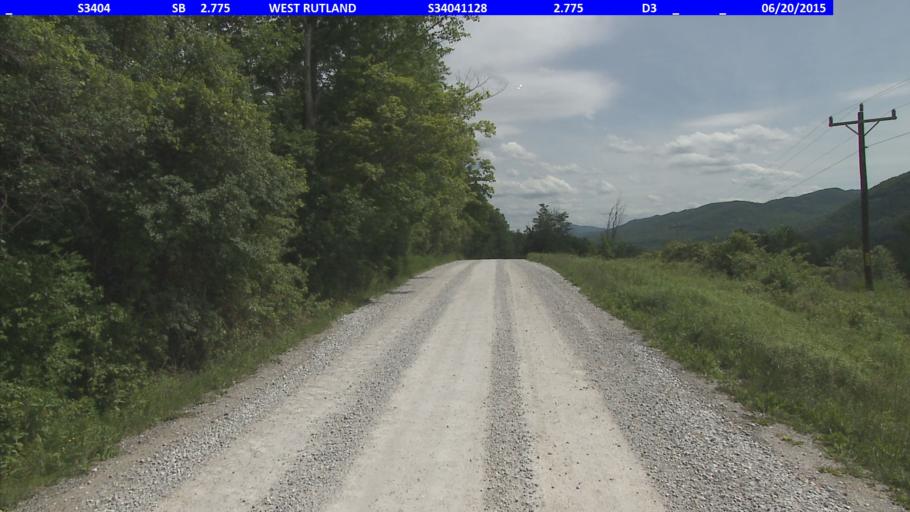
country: US
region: Vermont
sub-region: Rutland County
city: West Rutland
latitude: 43.6304
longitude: -73.0560
